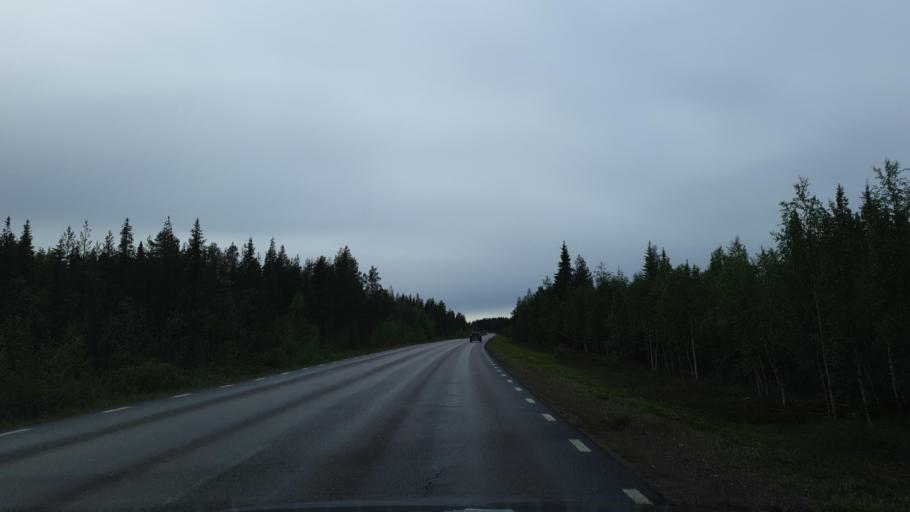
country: SE
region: Norrbotten
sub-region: Gallivare Kommun
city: Gaellivare
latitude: 67.1435
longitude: 20.7544
